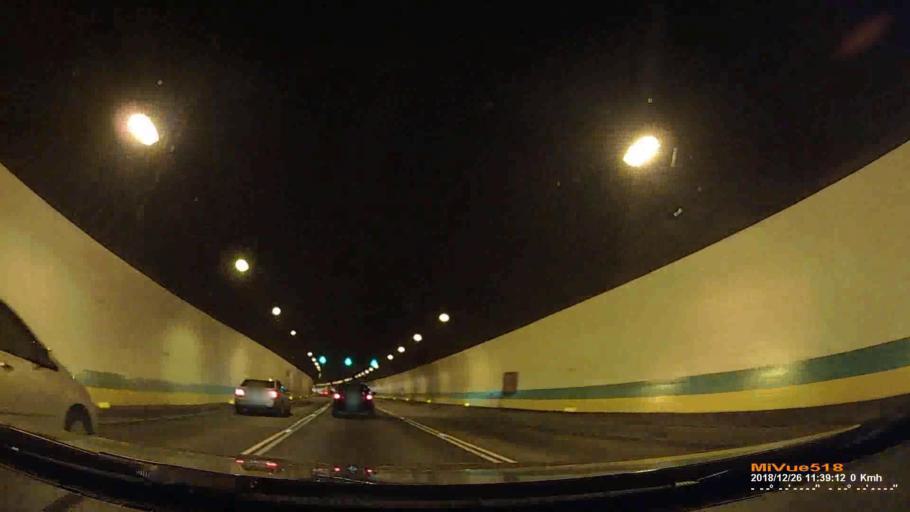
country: TW
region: Taipei
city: Taipei
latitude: 24.9885
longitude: 121.5904
